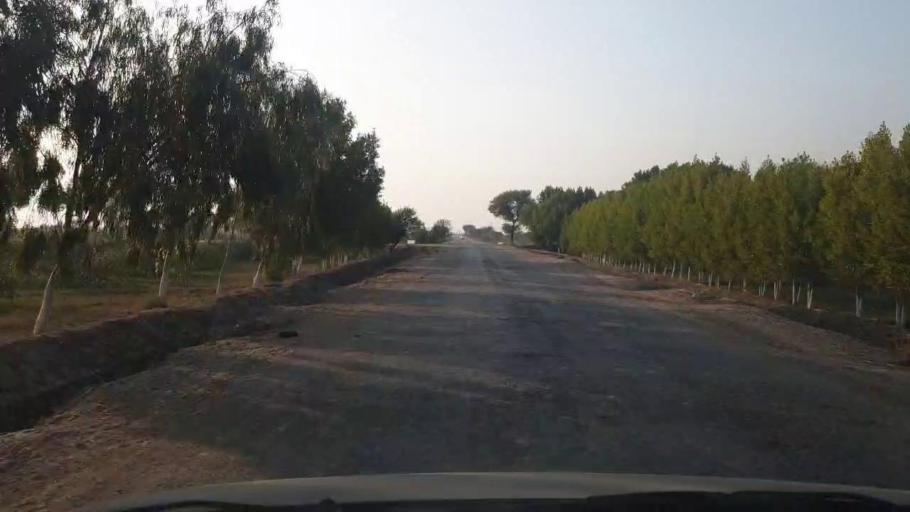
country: PK
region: Sindh
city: Mirwah Gorchani
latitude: 25.3659
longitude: 69.1411
